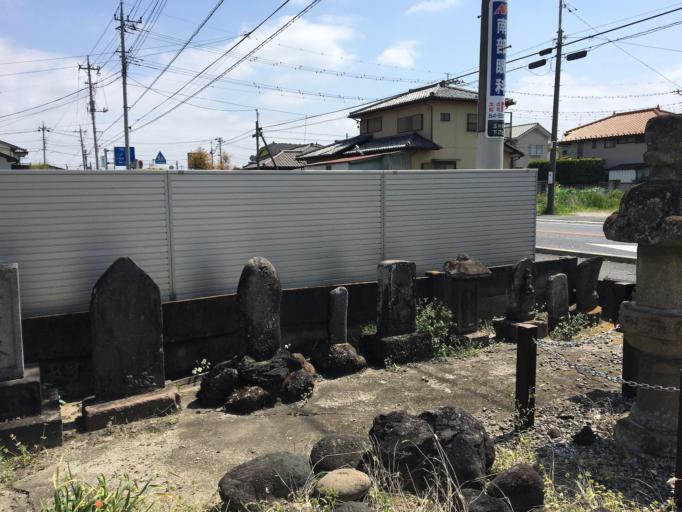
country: JP
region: Gunma
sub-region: Sawa-gun
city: Tamamura
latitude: 36.3028
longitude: 139.1242
